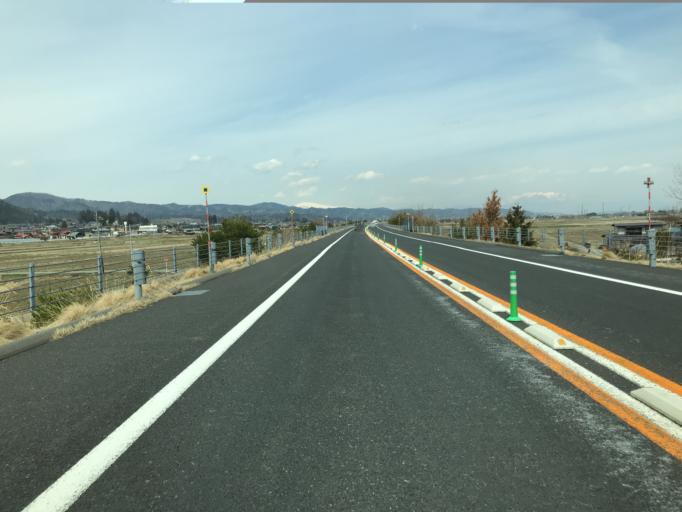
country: JP
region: Yamagata
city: Kaminoyama
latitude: 38.2257
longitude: 140.2786
